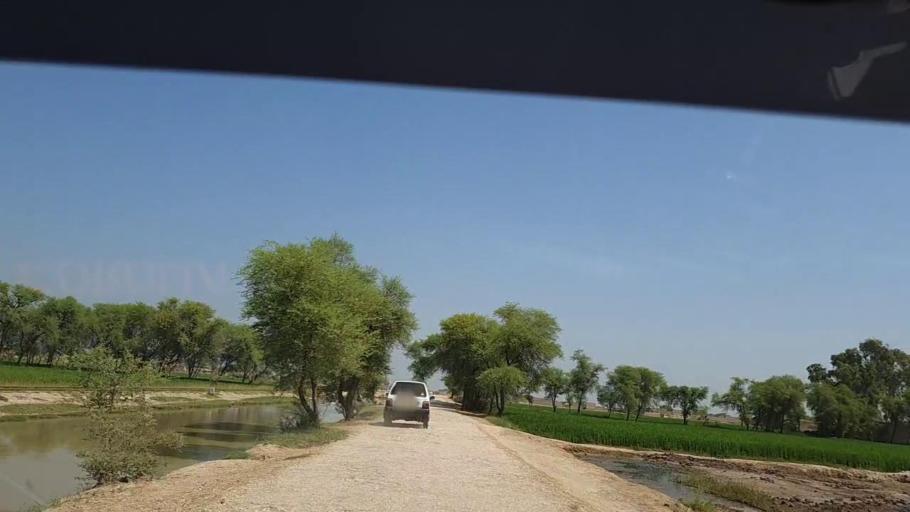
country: PK
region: Sindh
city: Tangwani
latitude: 28.2822
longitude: 69.0324
